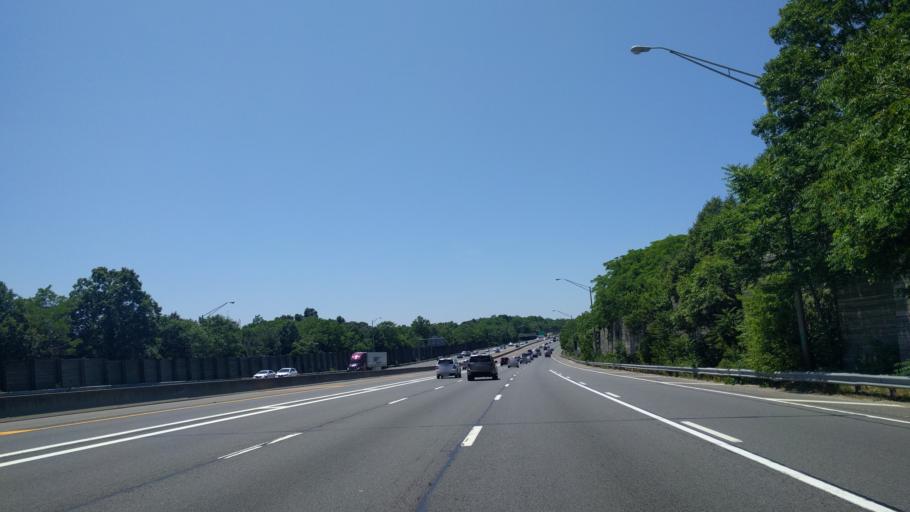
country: US
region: New York
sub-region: Suffolk County
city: Dix Hills
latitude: 40.7961
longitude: -73.3457
